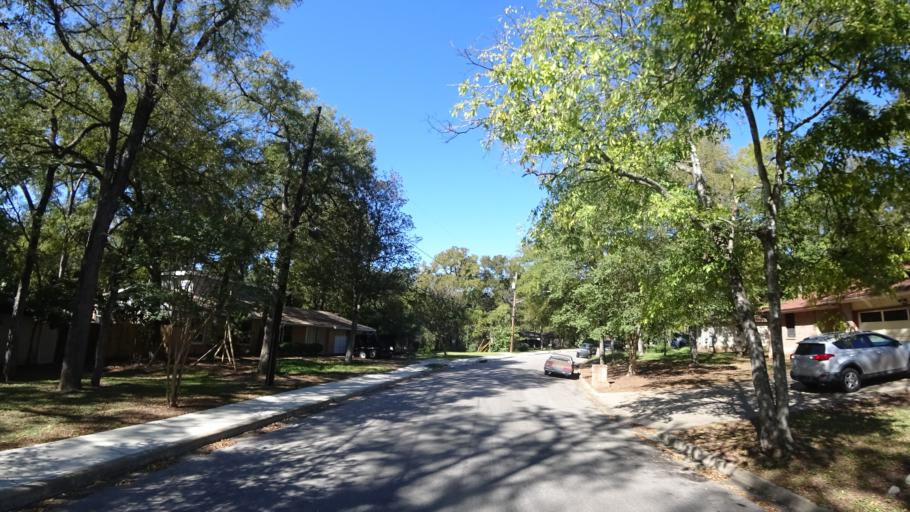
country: US
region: Texas
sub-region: Travis County
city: Austin
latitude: 30.2826
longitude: -97.6884
